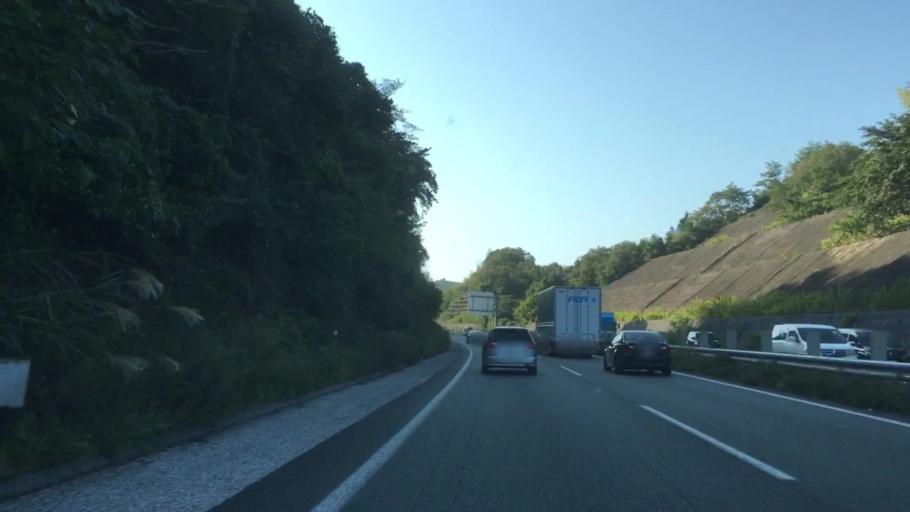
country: JP
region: Yamaguchi
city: Ogori-shimogo
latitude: 34.1278
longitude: 131.3822
